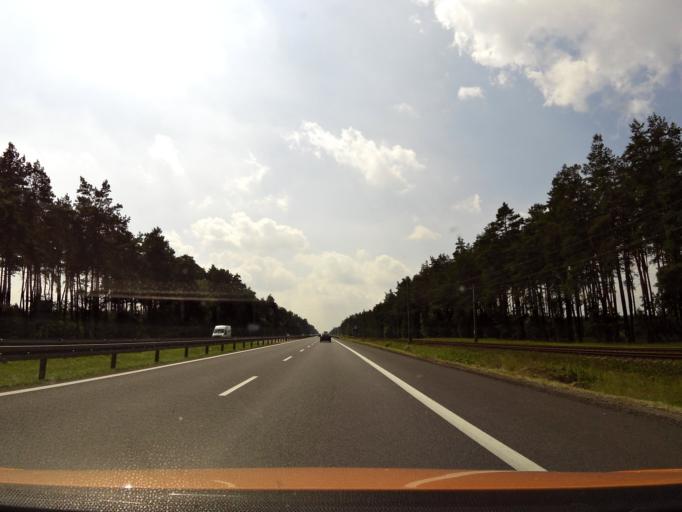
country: PL
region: West Pomeranian Voivodeship
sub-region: Powiat goleniowski
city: Goleniow
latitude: 53.5198
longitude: 14.8059
